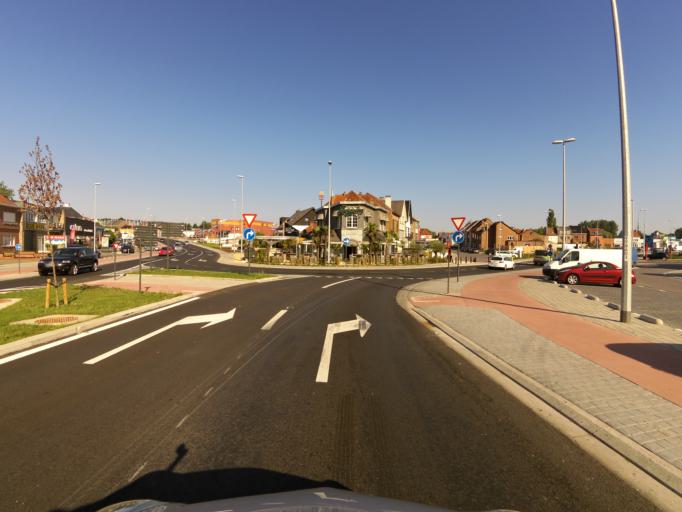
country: BE
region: Flanders
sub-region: Provincie Oost-Vlaanderen
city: Ninove
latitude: 50.8357
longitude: 4.0088
